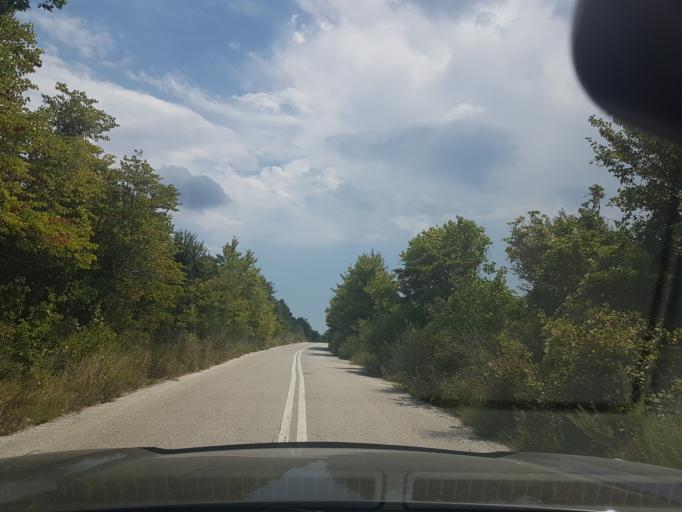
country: GR
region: Central Greece
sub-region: Nomos Evvoias
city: Kymi
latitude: 38.6461
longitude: 24.0492
